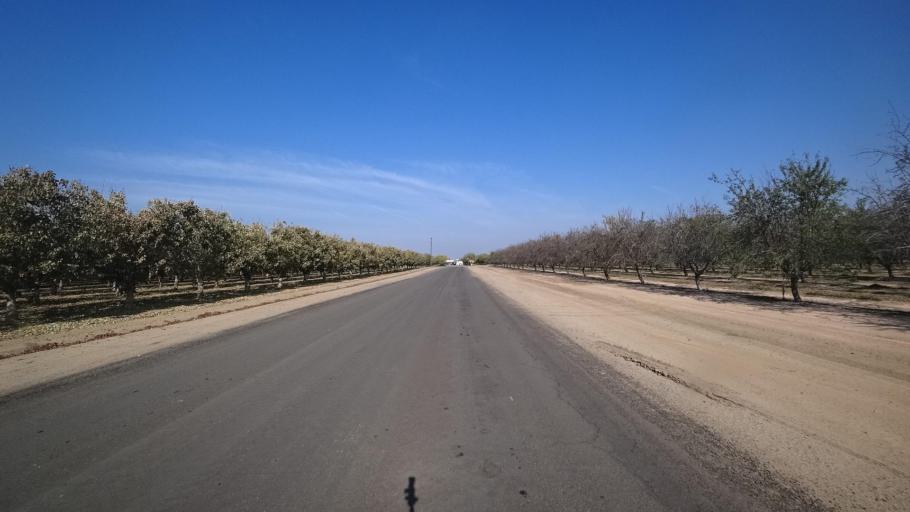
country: US
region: California
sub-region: Kern County
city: McFarland
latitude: 35.6588
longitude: -119.1868
